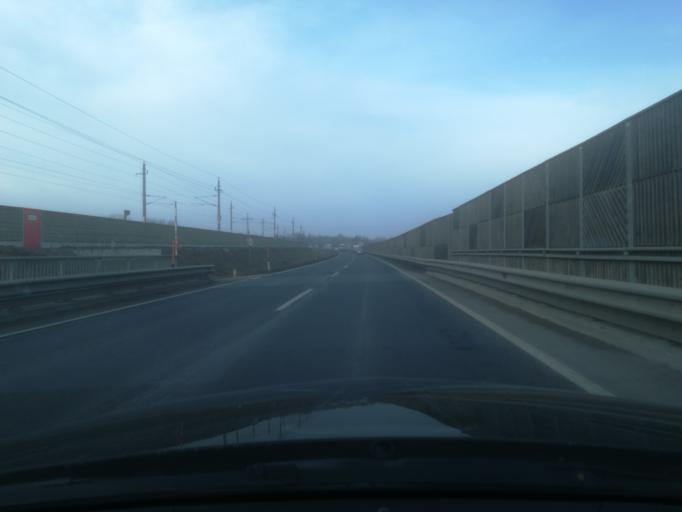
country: AT
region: Upper Austria
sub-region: Politischer Bezirk Linz-Land
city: Enns
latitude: 48.2266
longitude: 14.4877
